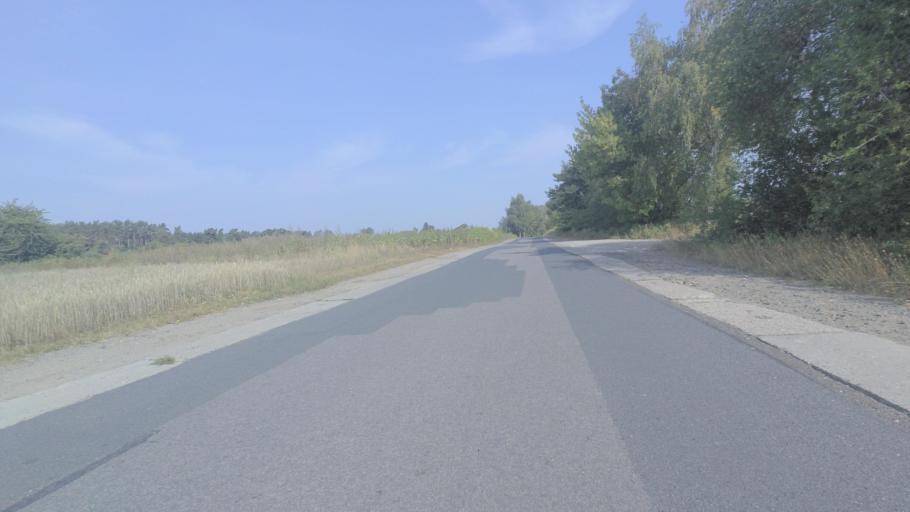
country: DE
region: Mecklenburg-Vorpommern
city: Wendorf
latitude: 54.2450
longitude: 13.0722
